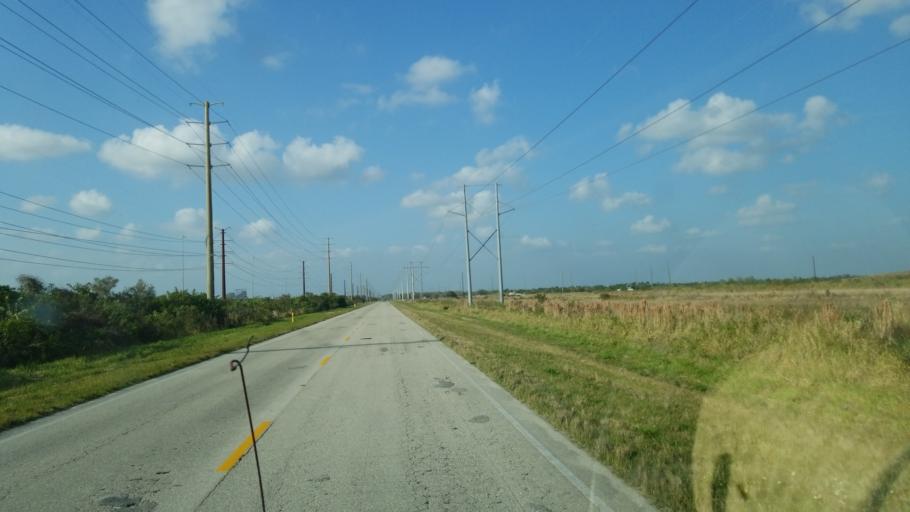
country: US
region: Florida
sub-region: Hardee County
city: Wauchula
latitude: 27.5679
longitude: -81.9346
